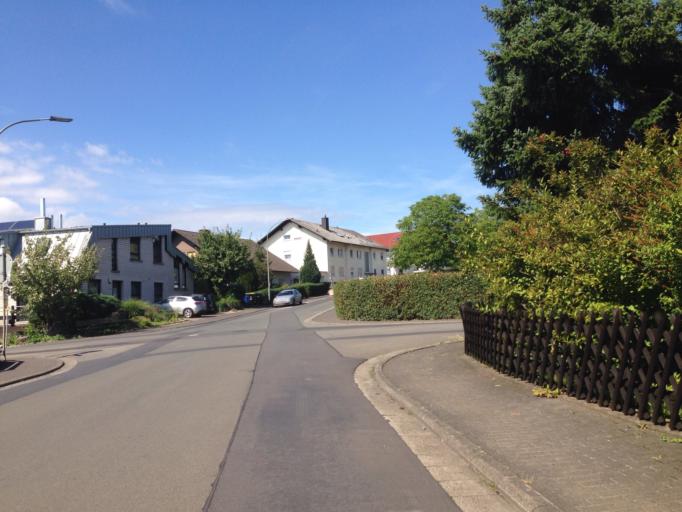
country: DE
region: Hesse
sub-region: Regierungsbezirk Giessen
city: Grunberg
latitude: 50.5926
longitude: 8.9488
